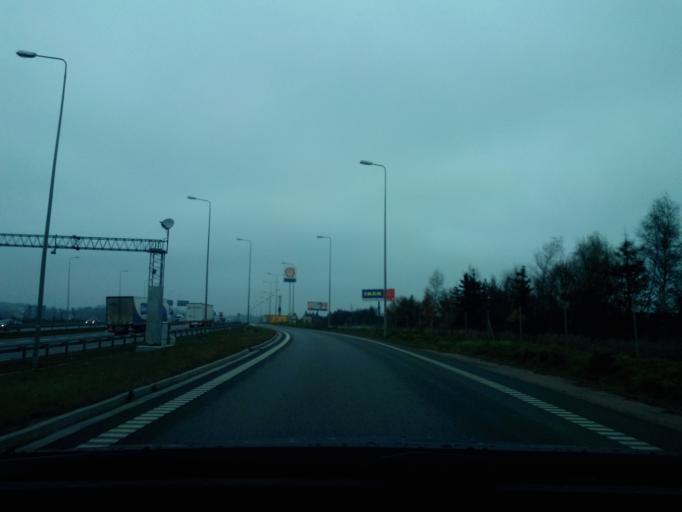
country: PL
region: Pomeranian Voivodeship
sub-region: Powiat gdanski
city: Kowale
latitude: 54.3641
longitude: 18.5203
